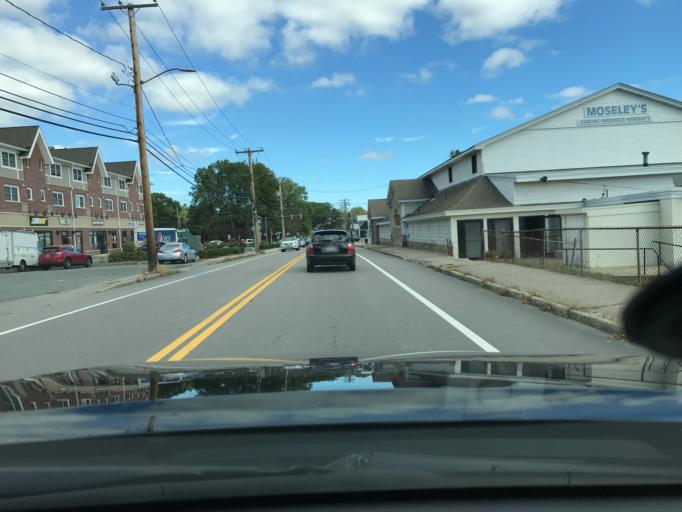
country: US
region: Massachusetts
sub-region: Norfolk County
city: Dedham
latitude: 42.2691
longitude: -71.1750
